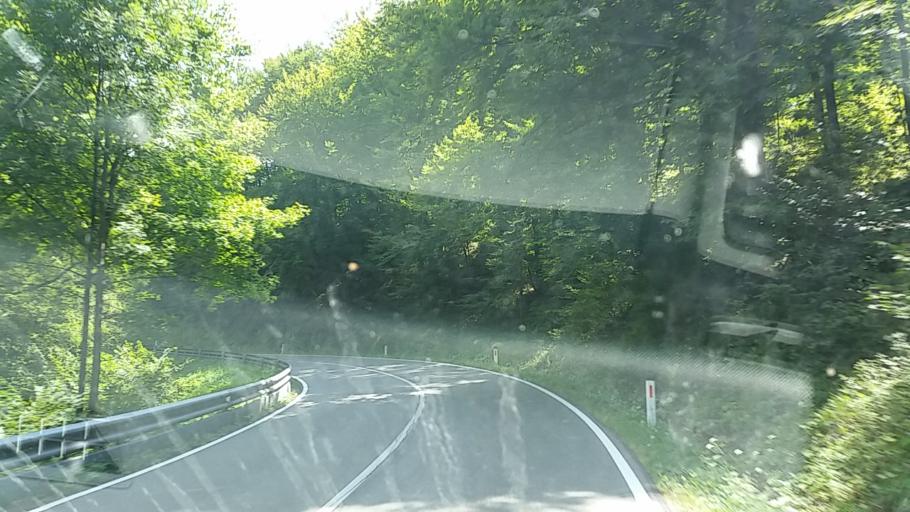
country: SI
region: Bovec
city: Bovec
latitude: 46.2867
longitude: 13.5264
